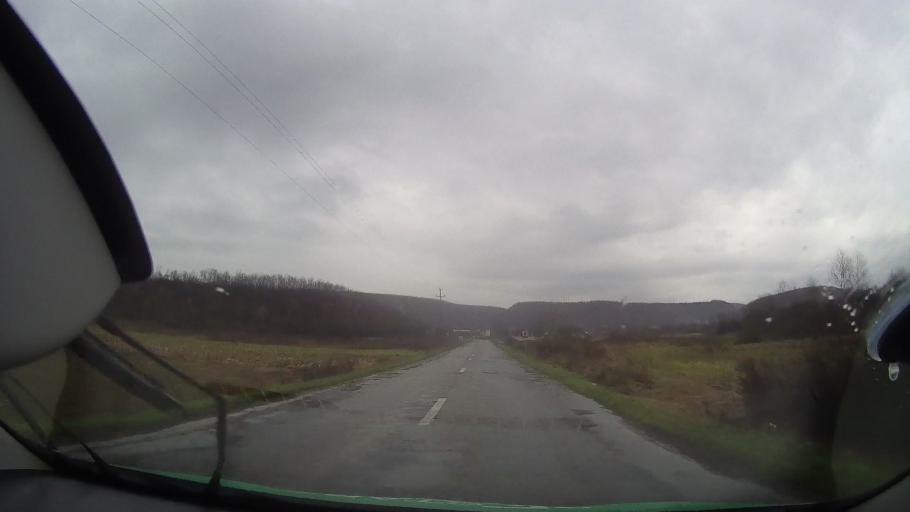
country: RO
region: Bihor
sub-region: Comuna Soimi
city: Soimi
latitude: 46.6853
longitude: 22.1098
